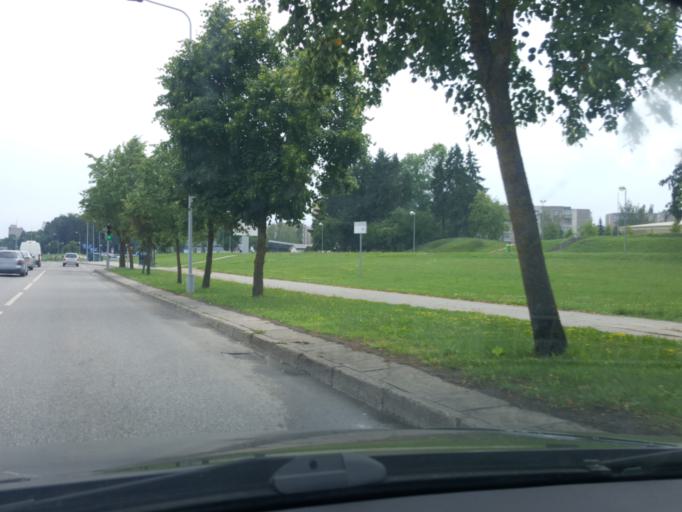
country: LT
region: Alytaus apskritis
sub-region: Alytus
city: Alytus
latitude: 54.4023
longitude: 24.0220
